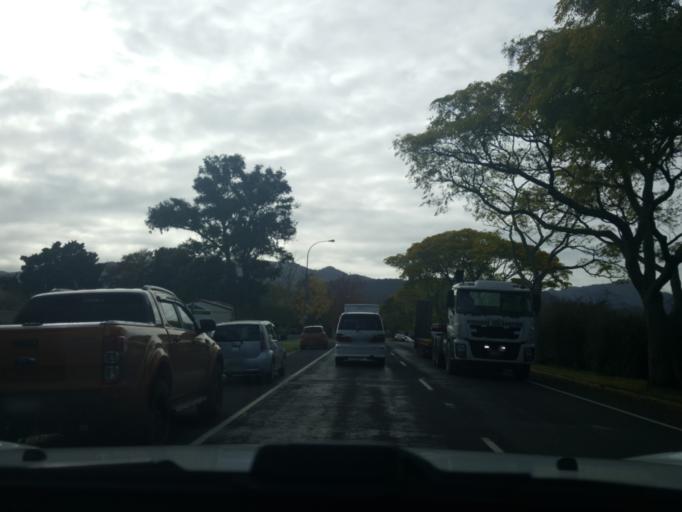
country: NZ
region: Waikato
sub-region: Hauraki District
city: Paeroa
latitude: -37.3859
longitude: 175.6690
